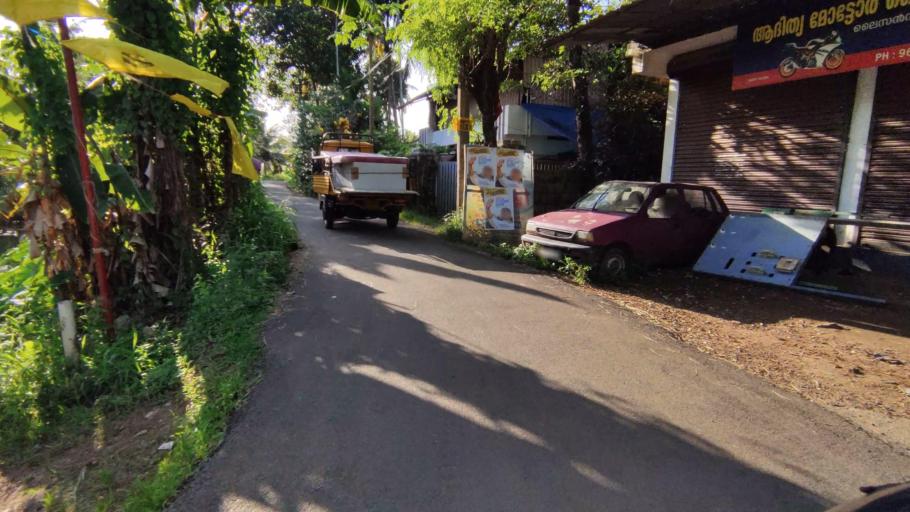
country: IN
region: Kerala
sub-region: Kottayam
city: Kottayam
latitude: 9.5969
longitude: 76.4873
